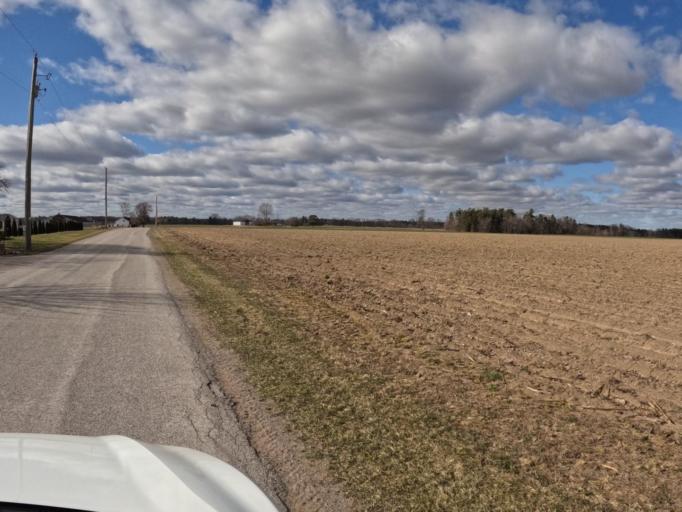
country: CA
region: Ontario
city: Norfolk County
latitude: 42.7471
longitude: -80.3835
